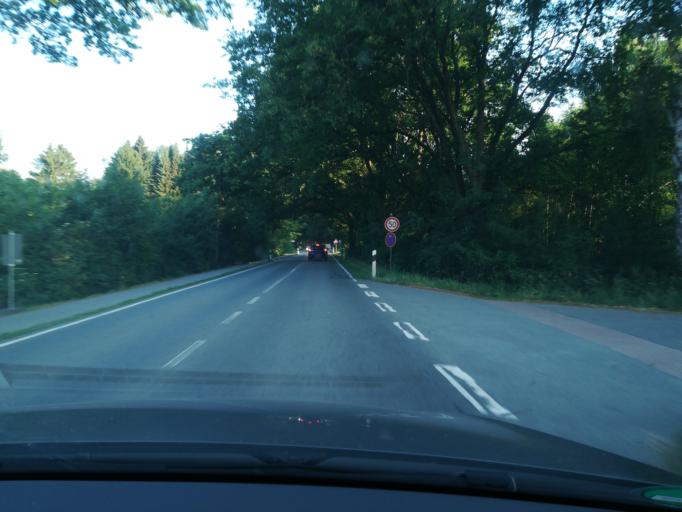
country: DE
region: Schleswig-Holstein
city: Grossensee
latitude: 53.6112
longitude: 10.3512
